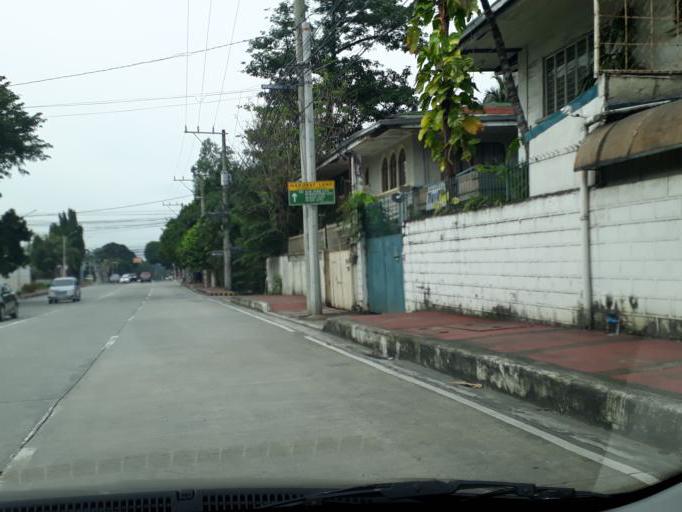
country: PH
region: Calabarzon
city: Del Monte
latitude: 14.6310
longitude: 121.0300
